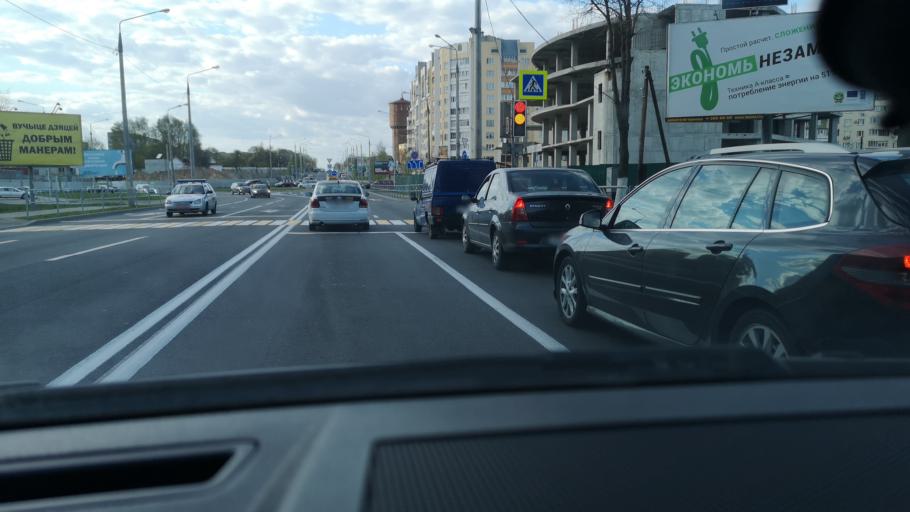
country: BY
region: Gomel
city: Gomel
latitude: 52.4387
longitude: 31.0000
